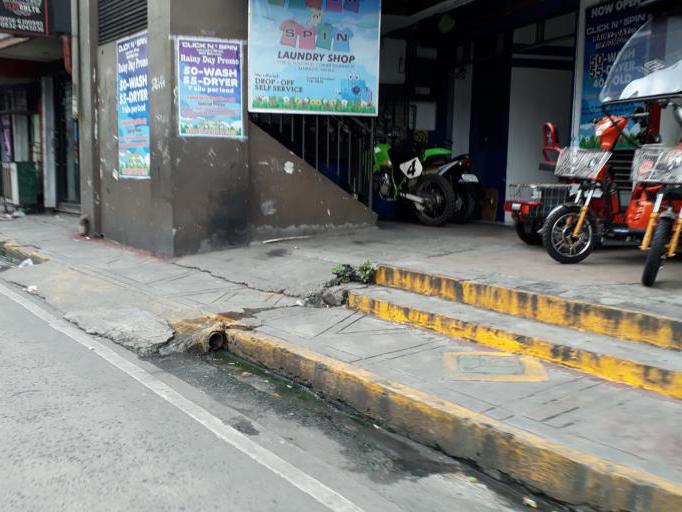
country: PH
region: Metro Manila
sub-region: City of Manila
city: Quiapo
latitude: 14.6071
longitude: 121.0033
